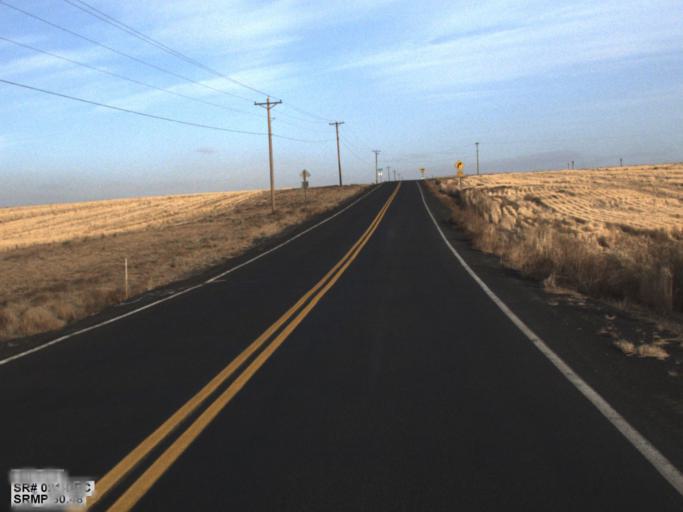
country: US
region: Washington
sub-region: Adams County
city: Ritzville
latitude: 47.2611
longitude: -118.6897
